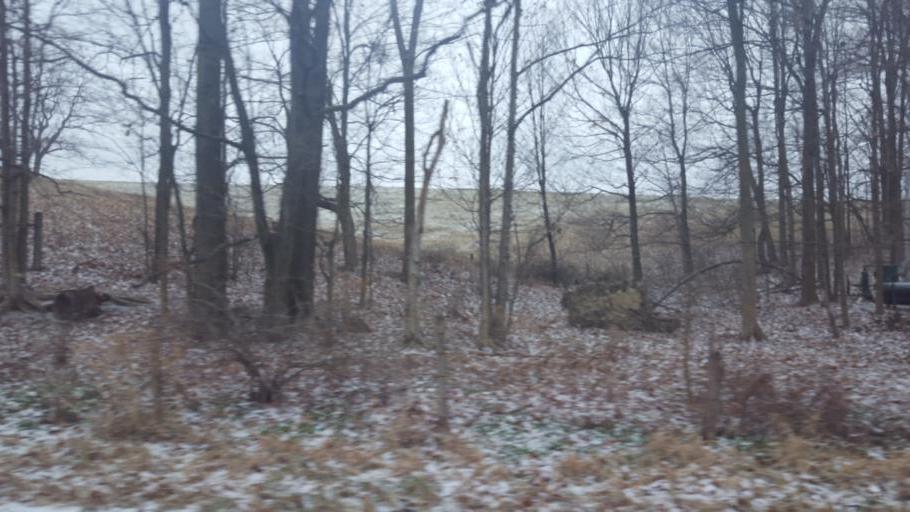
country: US
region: Ohio
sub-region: Tuscarawas County
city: Sugarcreek
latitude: 40.4568
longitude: -81.7474
